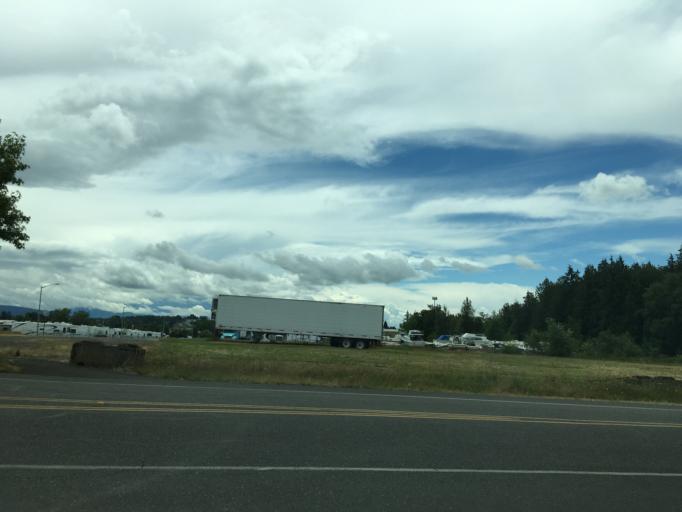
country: US
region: Washington
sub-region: Whatcom County
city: Lynden
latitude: 48.9389
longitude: -122.4885
